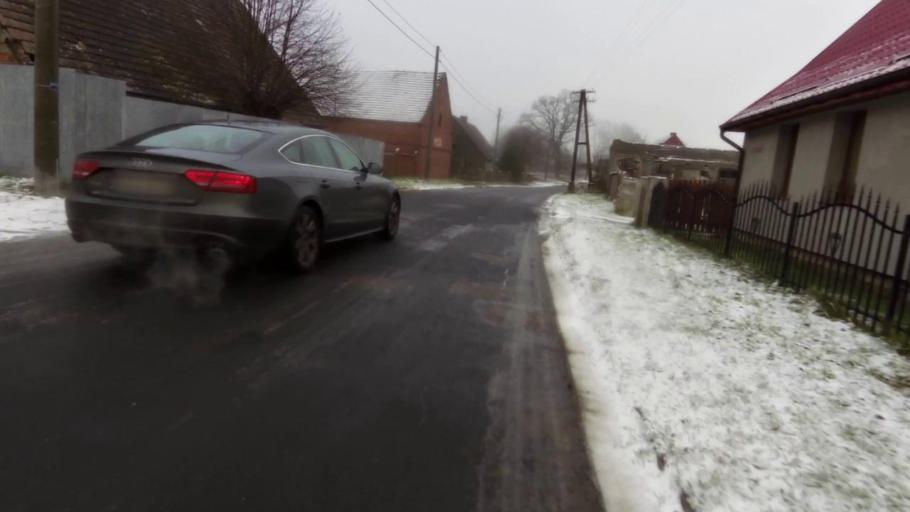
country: PL
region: West Pomeranian Voivodeship
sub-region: Powiat drawski
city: Wierzchowo
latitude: 53.4436
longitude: 16.1635
